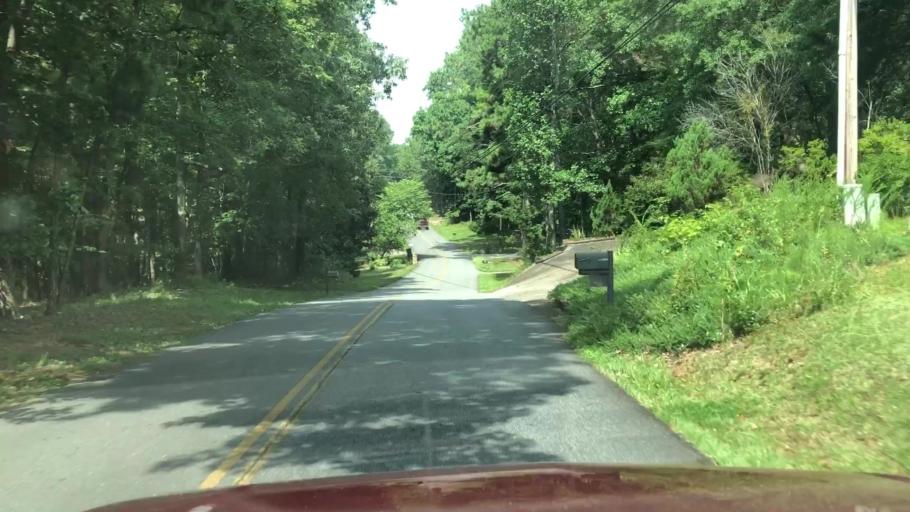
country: US
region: Georgia
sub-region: Cherokee County
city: Woodstock
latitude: 34.1487
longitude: -84.6098
